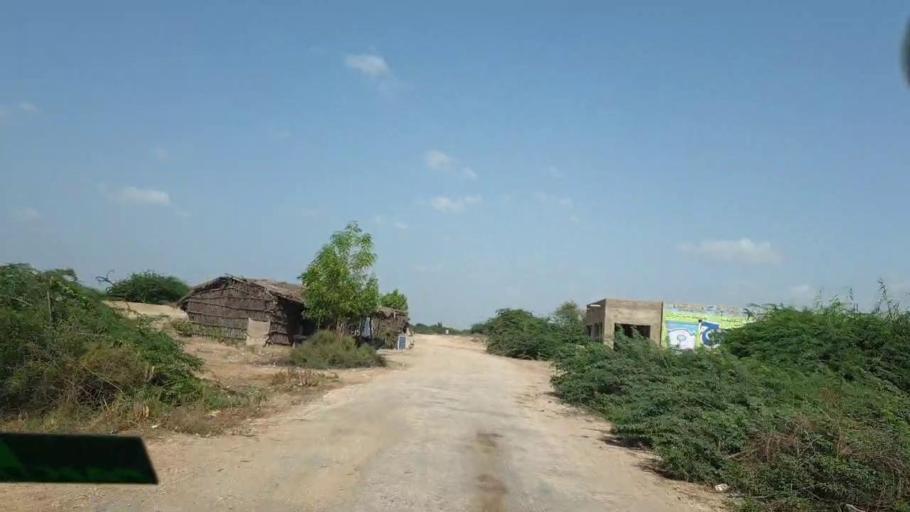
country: PK
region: Sindh
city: Tando Bago
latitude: 24.6745
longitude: 69.1948
